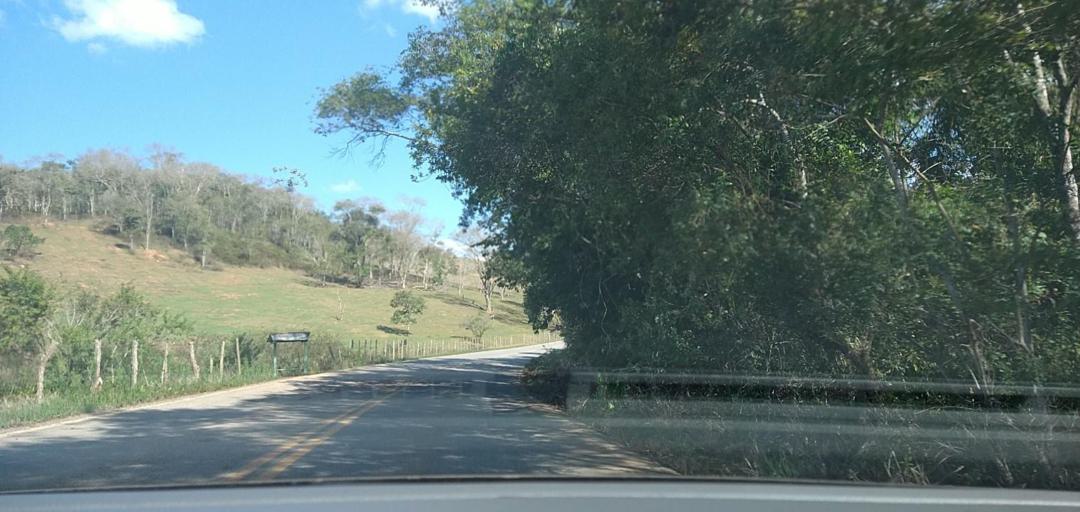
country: BR
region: Minas Gerais
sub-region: Alvinopolis
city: Alvinopolis
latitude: -20.0315
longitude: -43.0479
